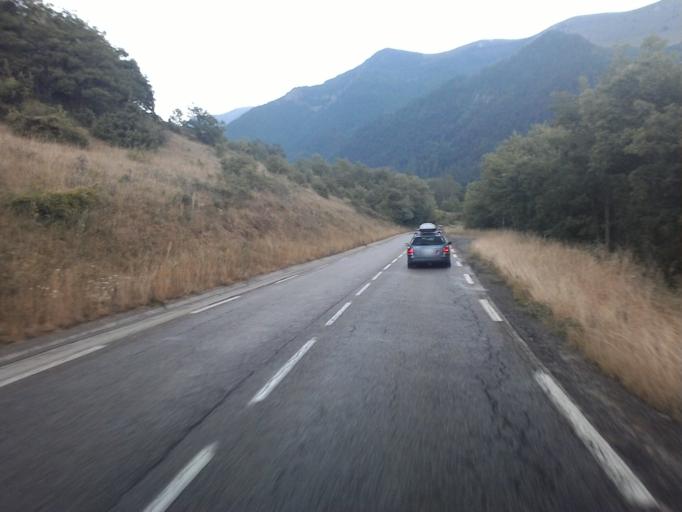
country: FR
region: Rhone-Alpes
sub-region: Departement de l'Isere
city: La Mure
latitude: 44.8245
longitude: 5.9419
